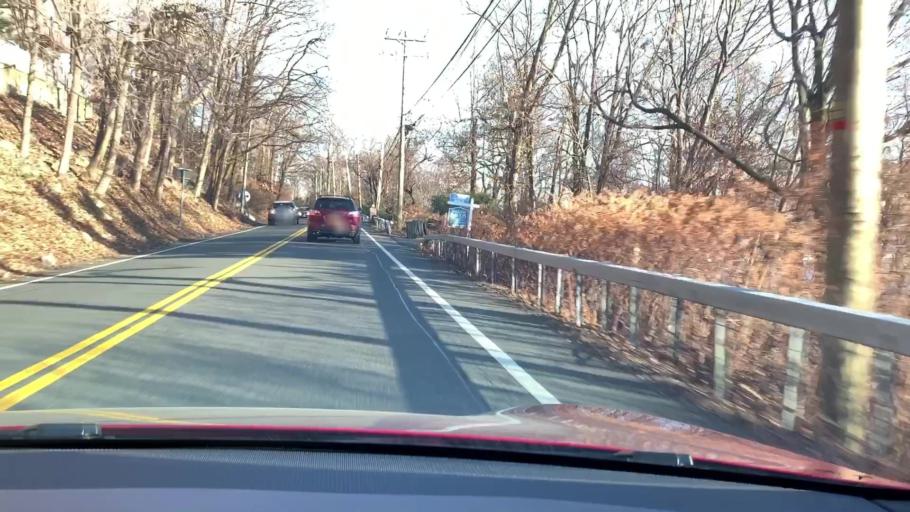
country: US
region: New York
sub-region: Rockland County
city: Piermont
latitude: 41.0572
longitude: -73.9231
